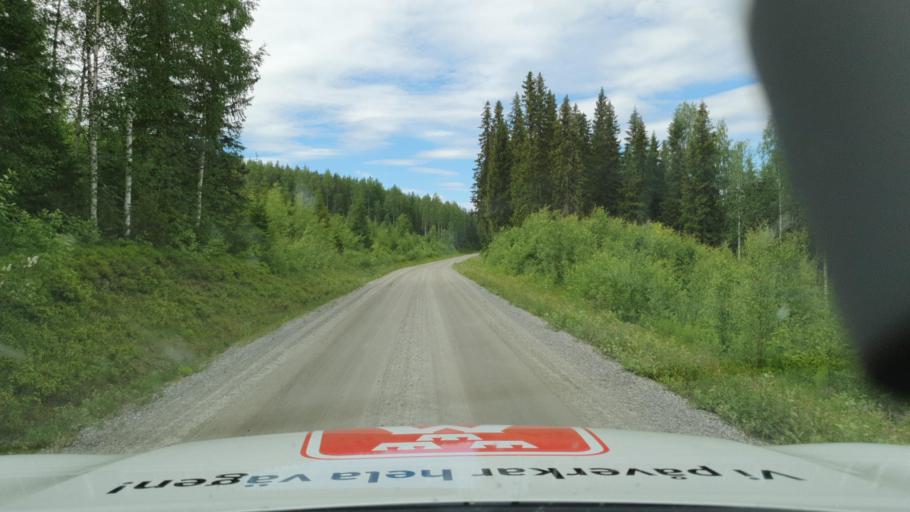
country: SE
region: Vaesterbotten
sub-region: Norsjo Kommun
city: Norsjoe
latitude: 64.7979
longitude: 19.6674
